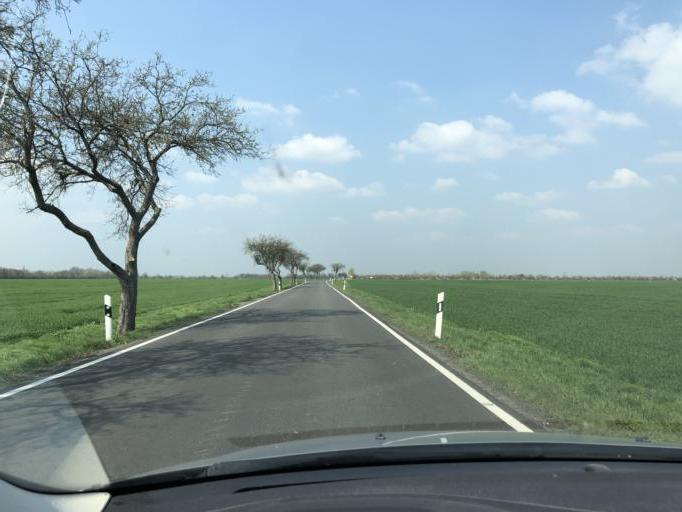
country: DE
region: Saxony
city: Wiedemar
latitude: 51.4900
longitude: 12.2157
